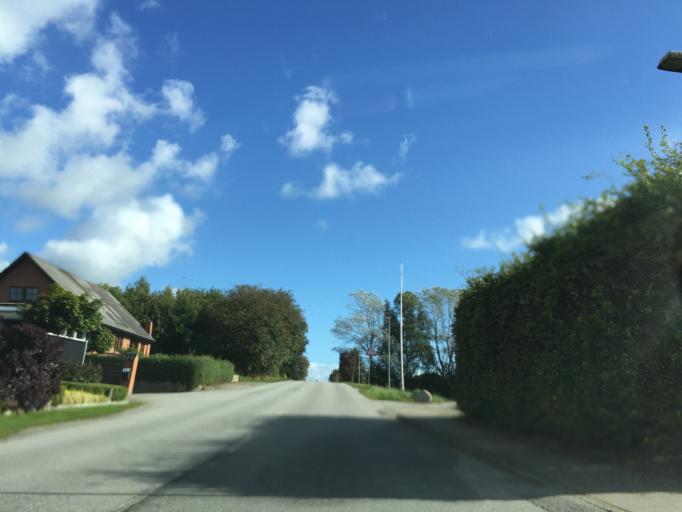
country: DK
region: Central Jutland
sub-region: Viborg Kommune
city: Viborg
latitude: 56.4417
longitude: 9.4893
